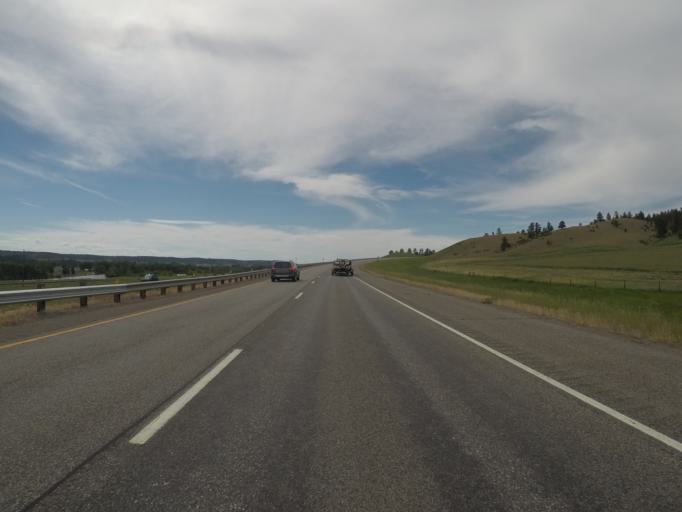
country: US
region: Montana
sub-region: Stillwater County
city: Columbus
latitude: 45.6059
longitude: -109.1606
